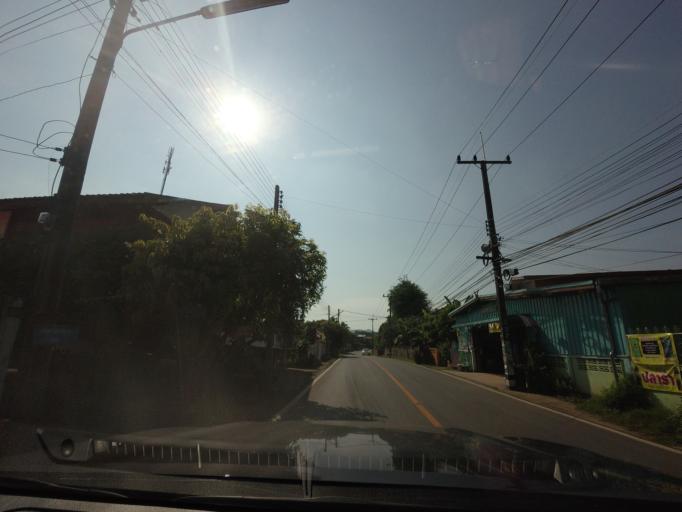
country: TH
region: Nan
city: Nan
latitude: 18.8577
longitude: 100.8153
